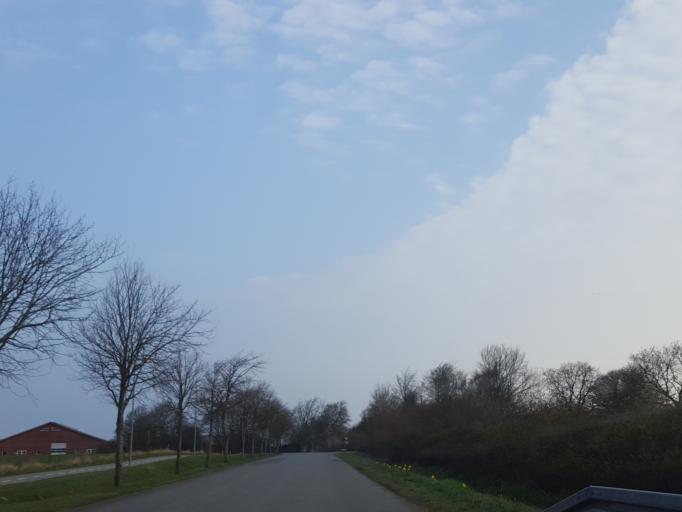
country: DK
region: South Denmark
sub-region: Esbjerg Kommune
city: Bramming
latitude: 55.4833
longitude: 8.7028
